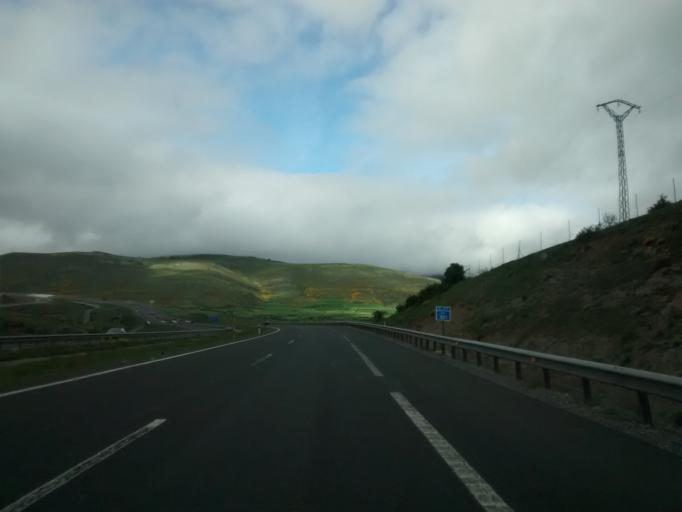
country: ES
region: Cantabria
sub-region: Provincia de Cantabria
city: Mataporquera
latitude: 42.8989
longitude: -4.1224
